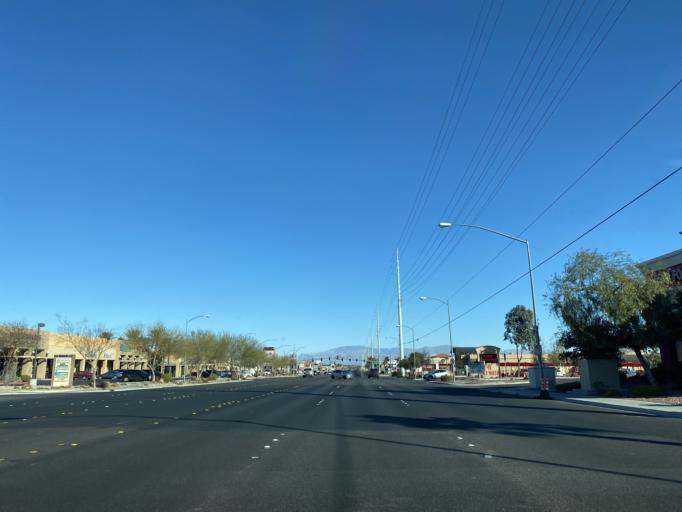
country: US
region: Nevada
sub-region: Clark County
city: Spring Valley
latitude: 36.0757
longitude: -115.2425
